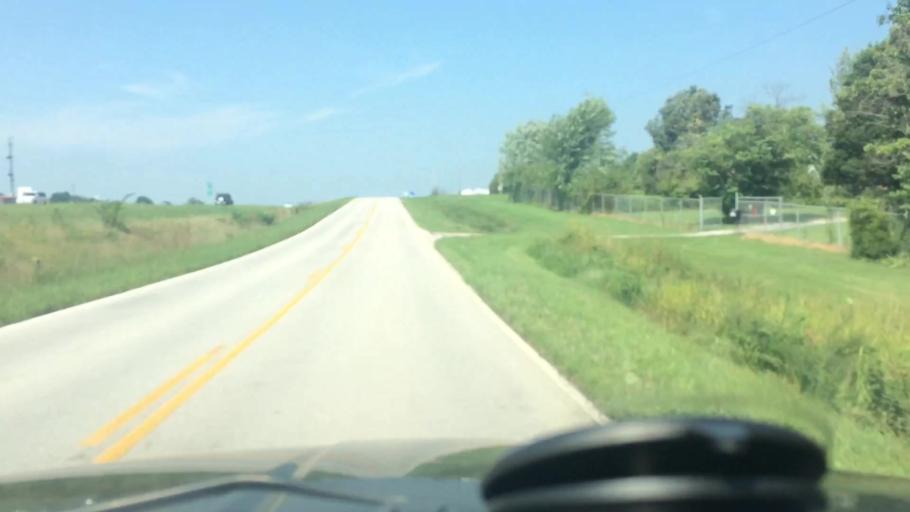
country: US
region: Missouri
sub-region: Greene County
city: Strafford
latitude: 37.2710
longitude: -93.0796
